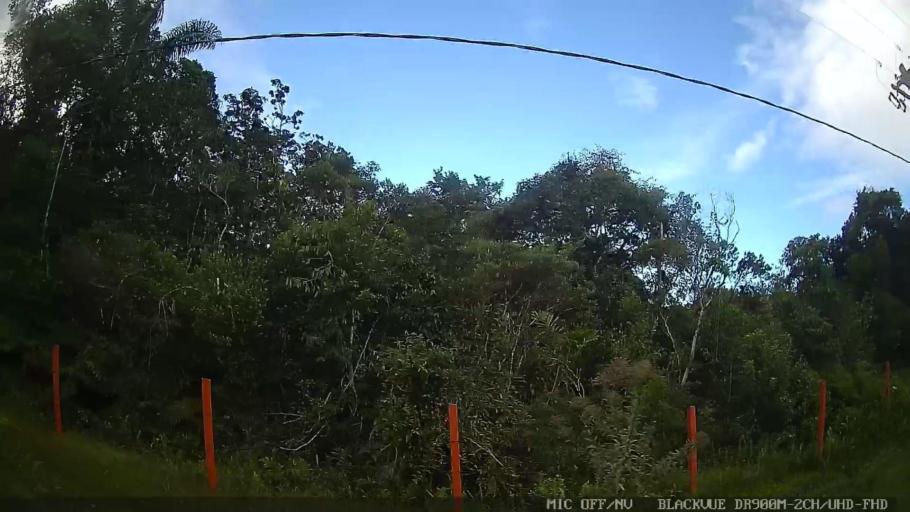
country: BR
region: Sao Paulo
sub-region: Peruibe
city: Peruibe
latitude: -24.1845
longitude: -46.9402
